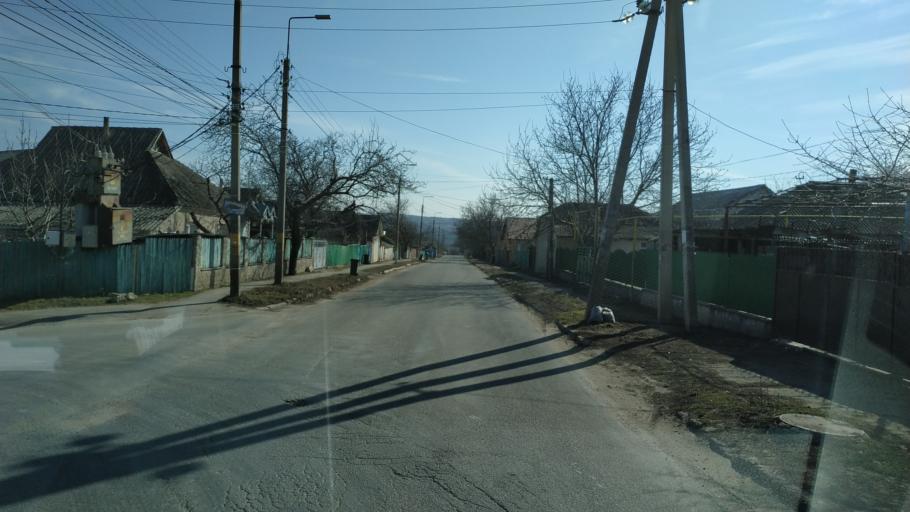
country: MD
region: Nisporeni
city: Nisporeni
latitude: 47.0715
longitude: 28.1704
